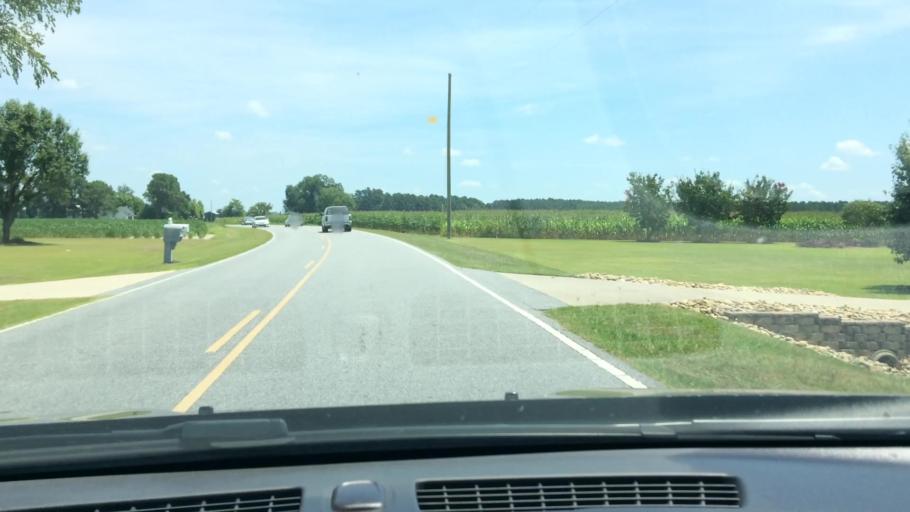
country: US
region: North Carolina
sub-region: Pitt County
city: Windsor
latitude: 35.5383
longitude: -77.2993
